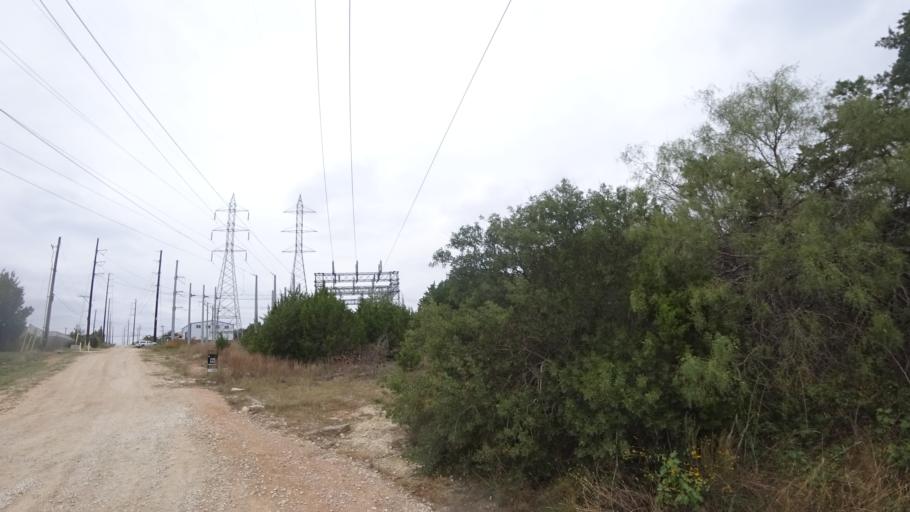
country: US
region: Texas
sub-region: Travis County
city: Lakeway
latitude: 30.3780
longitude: -97.9418
